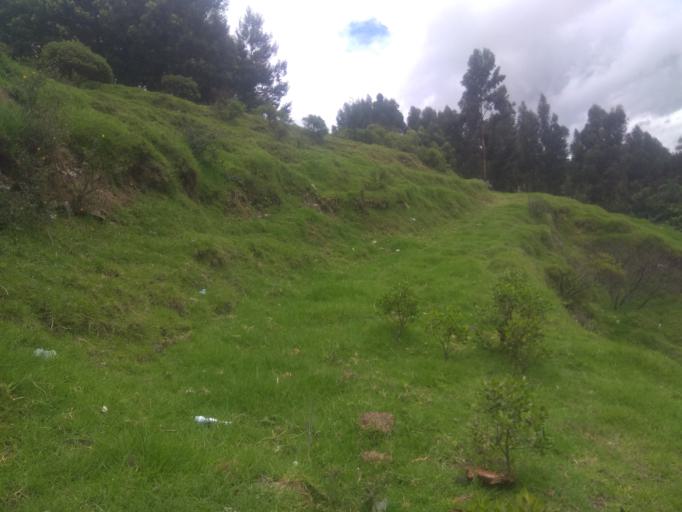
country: CO
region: Boyaca
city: Socota
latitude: 6.0175
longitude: -72.6586
